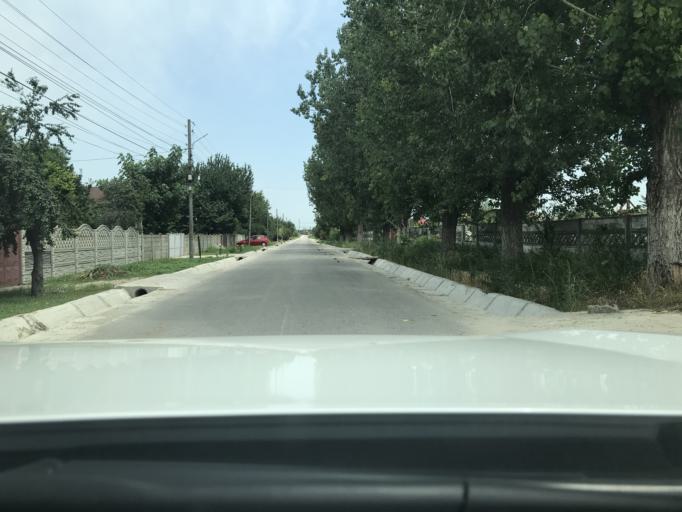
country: RO
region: Olt
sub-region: Comuna Osica de Sus
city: Osica de Sus
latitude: 44.2575
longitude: 24.3166
